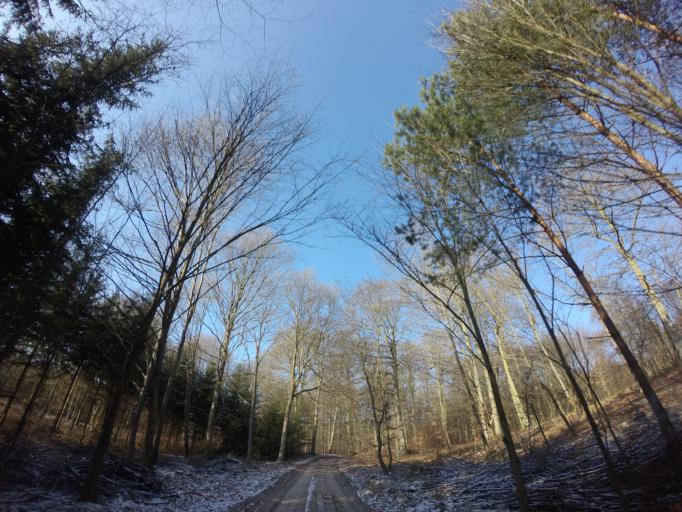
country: PL
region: West Pomeranian Voivodeship
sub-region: Powiat choszczenski
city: Pelczyce
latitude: 52.9489
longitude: 15.3402
